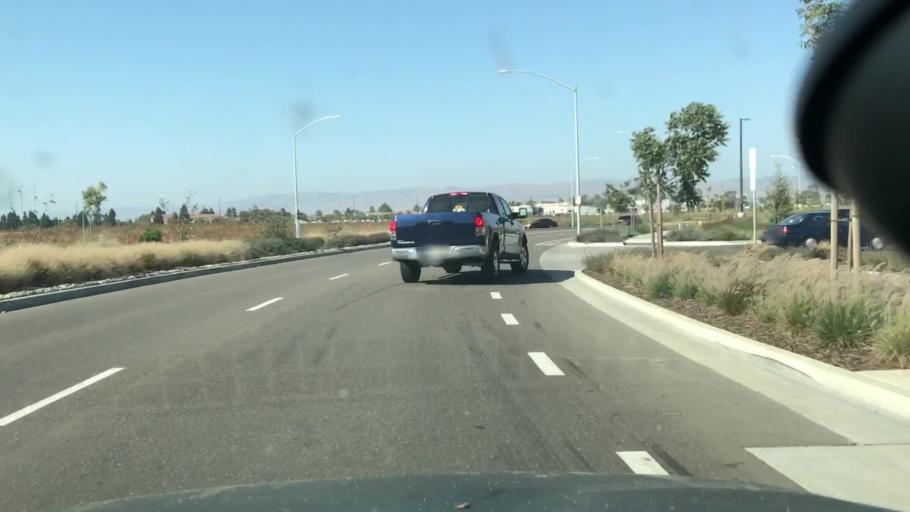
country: US
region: California
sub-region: Santa Barbara County
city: Santa Maria
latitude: 34.9262
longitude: -120.4219
